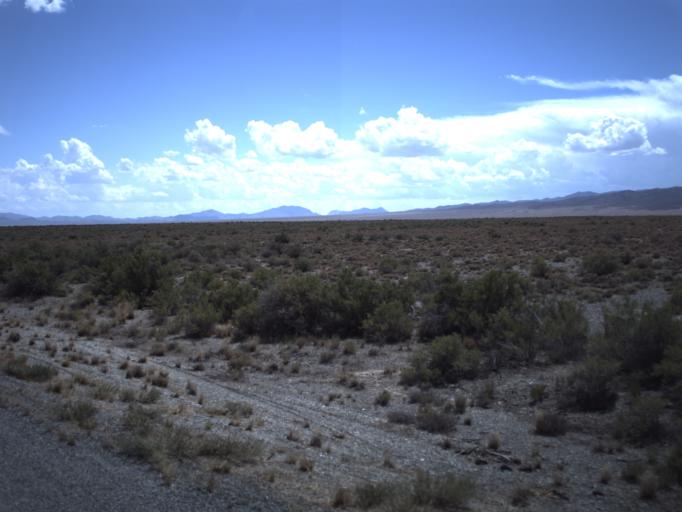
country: US
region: Nevada
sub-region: White Pine County
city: McGill
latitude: 39.0504
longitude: -113.9616
